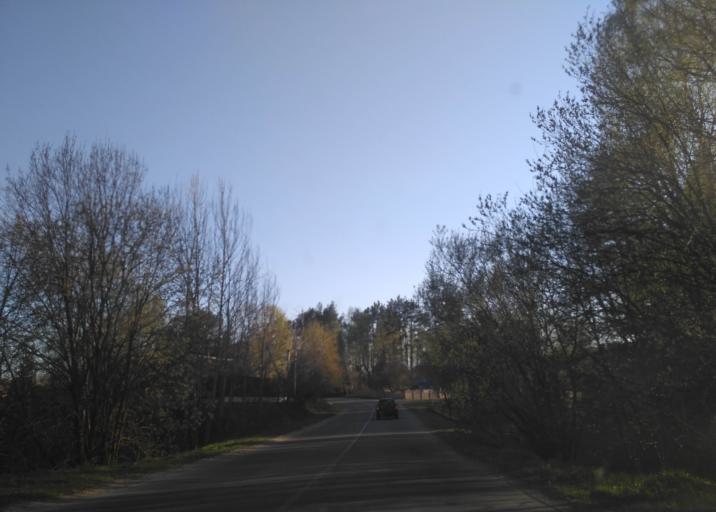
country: BY
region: Minsk
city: Pyatryshki
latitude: 54.1177
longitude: 27.1939
